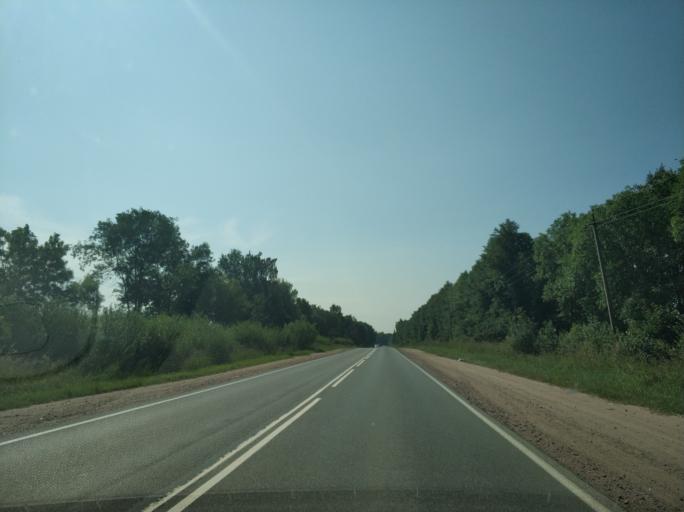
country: RU
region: Leningrad
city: Romanovka
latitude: 60.0669
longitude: 30.7412
